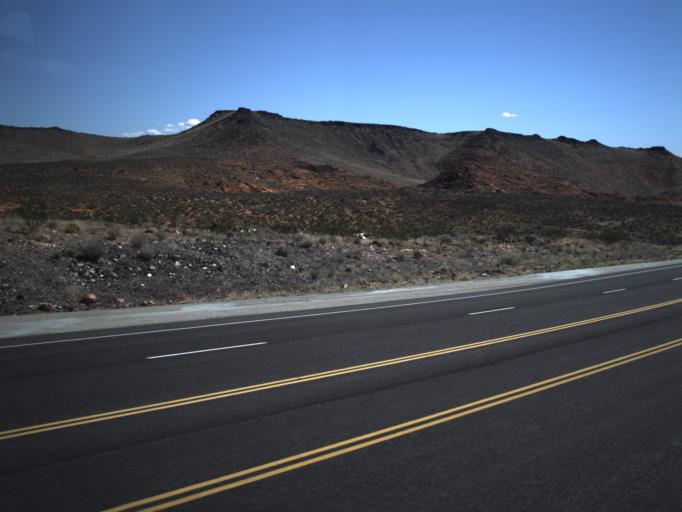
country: US
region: Utah
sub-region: Washington County
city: Santa Clara
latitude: 37.1698
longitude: -113.6179
